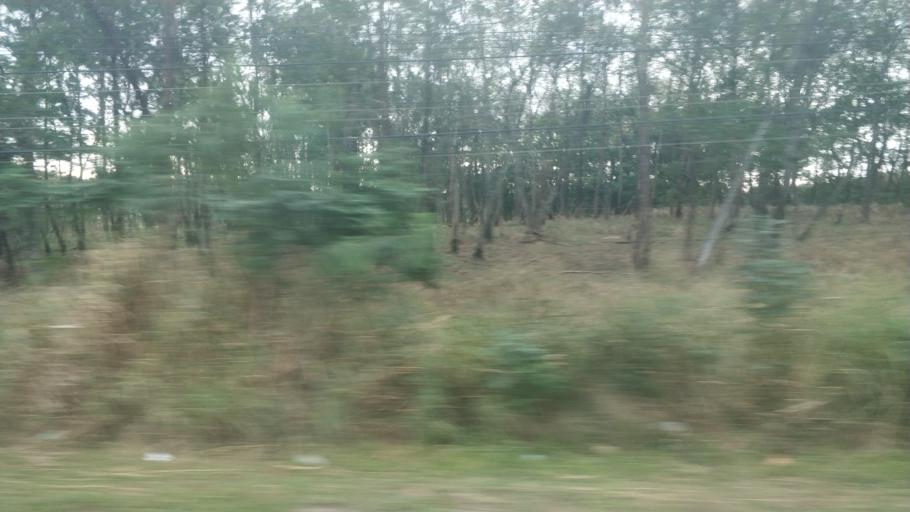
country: BR
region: Rio de Janeiro
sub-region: Seropedica
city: Seropedica
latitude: -22.7555
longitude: -43.6917
